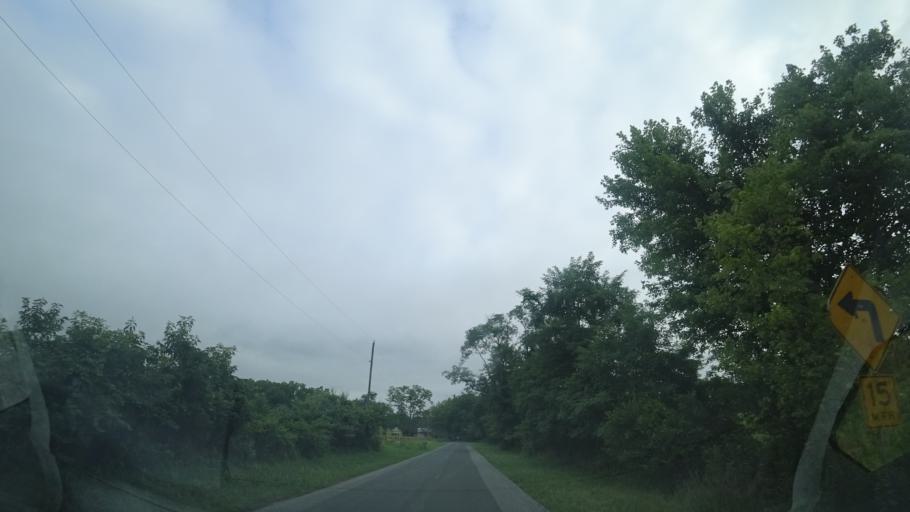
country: US
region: Maryland
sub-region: Montgomery County
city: Poolesville
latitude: 39.1122
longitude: -77.4473
